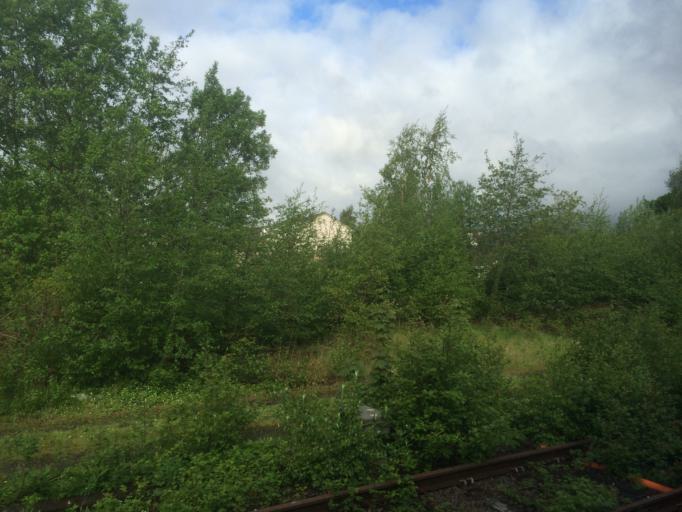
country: GB
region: Scotland
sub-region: Perth and Kinross
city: Perth
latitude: 56.3879
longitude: -3.4369
